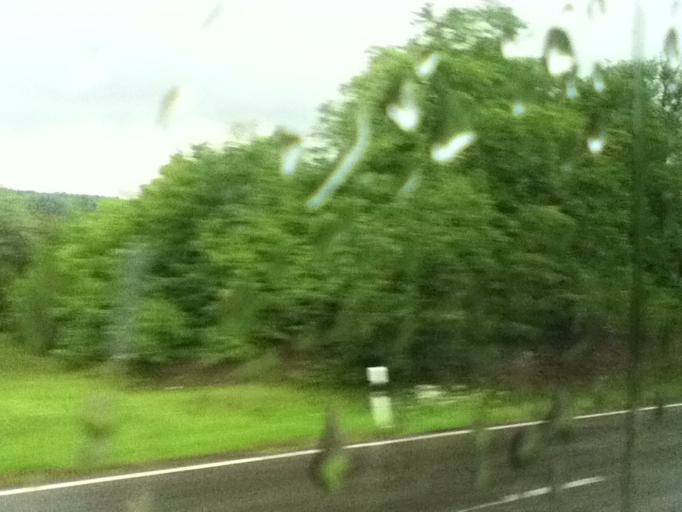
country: DE
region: Thuringia
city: Gera
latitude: 50.9082
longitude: 12.0684
